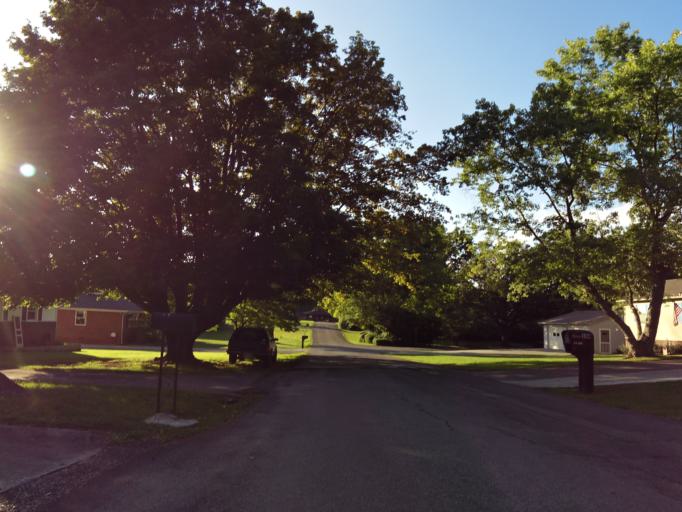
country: US
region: Tennessee
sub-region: Blount County
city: Eagleton Village
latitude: 35.7979
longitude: -83.9469
